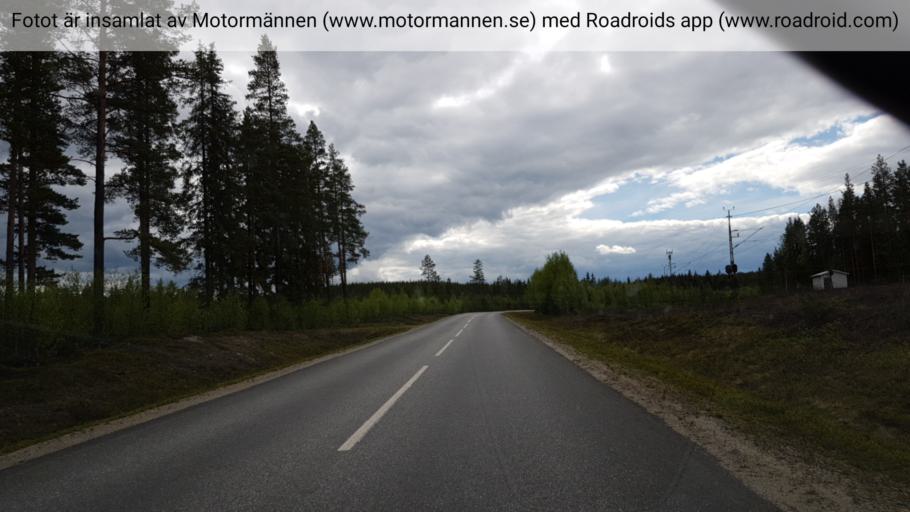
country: SE
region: Vaesterbotten
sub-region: Vindelns Kommun
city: Vindeln
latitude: 64.3618
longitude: 19.6563
